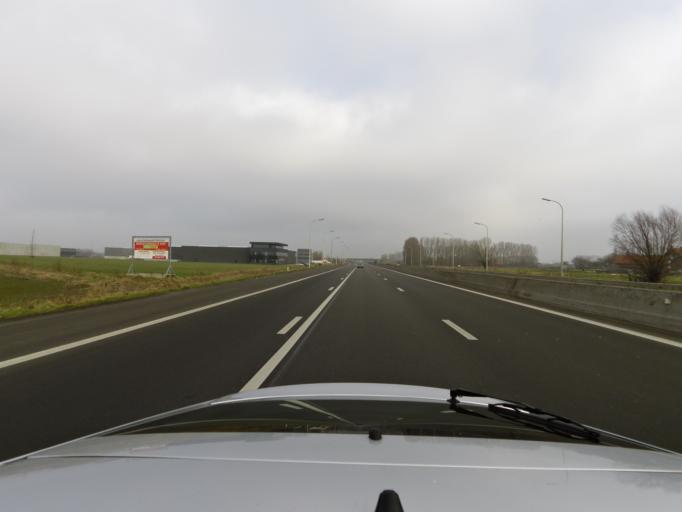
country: BE
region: Flanders
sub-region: Provincie West-Vlaanderen
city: Ardooie
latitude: 50.9664
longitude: 3.1776
